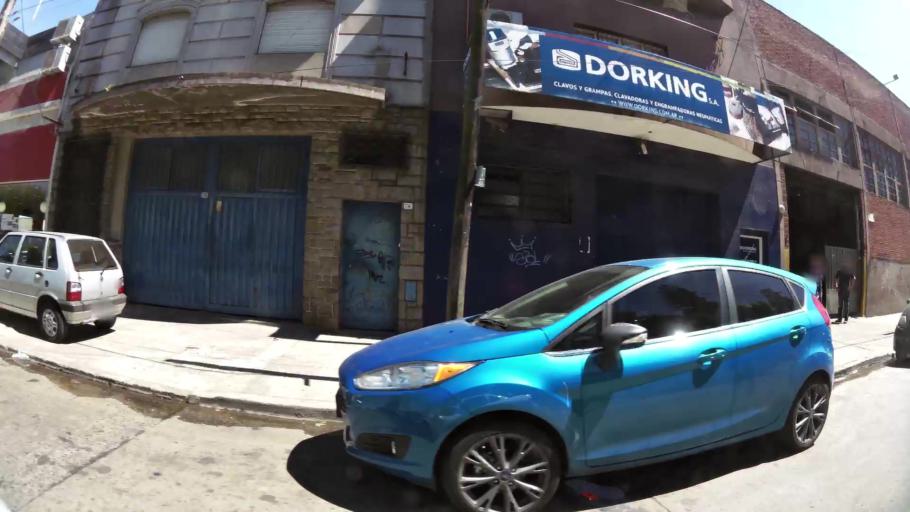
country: AR
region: Buenos Aires
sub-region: Partido de General San Martin
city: General San Martin
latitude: -34.5870
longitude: -58.5255
